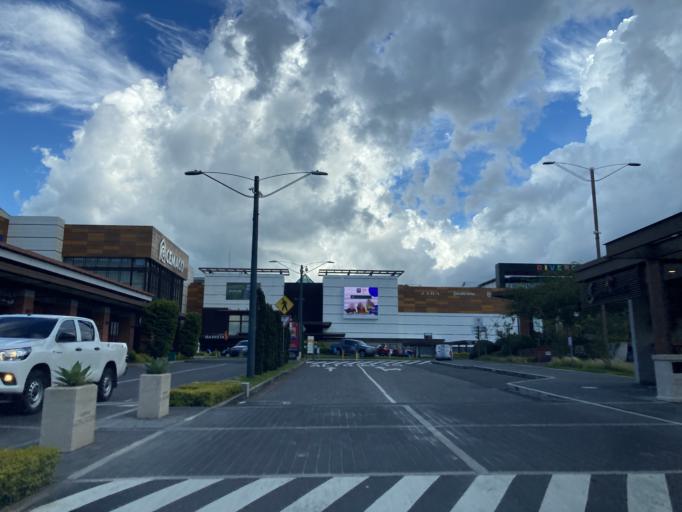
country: GT
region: Guatemala
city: San Jose Pinula
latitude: 14.5532
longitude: -90.4541
